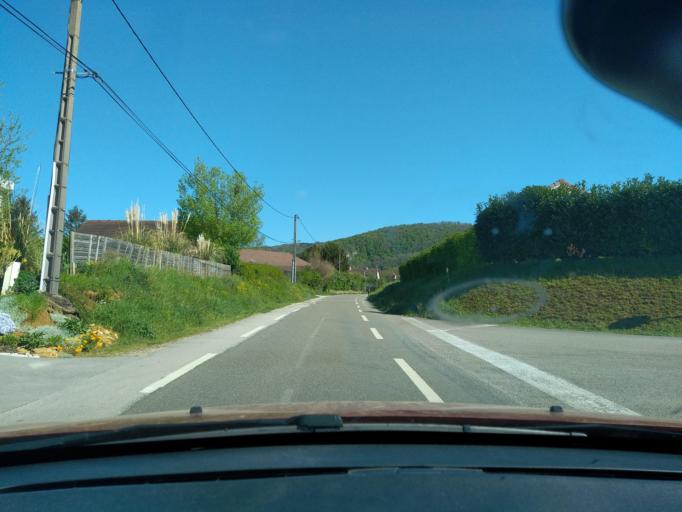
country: FR
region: Franche-Comte
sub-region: Departement du Jura
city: Cousance
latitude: 46.5778
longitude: 5.4358
